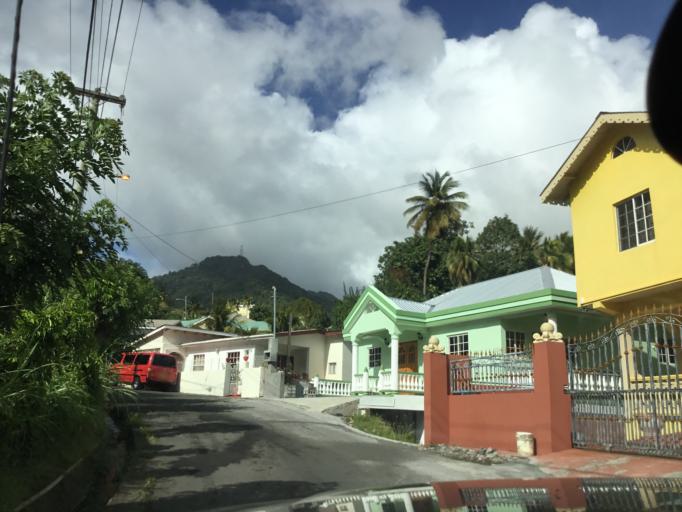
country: VC
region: Saint George
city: Kingstown
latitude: 13.1688
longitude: -61.2200
